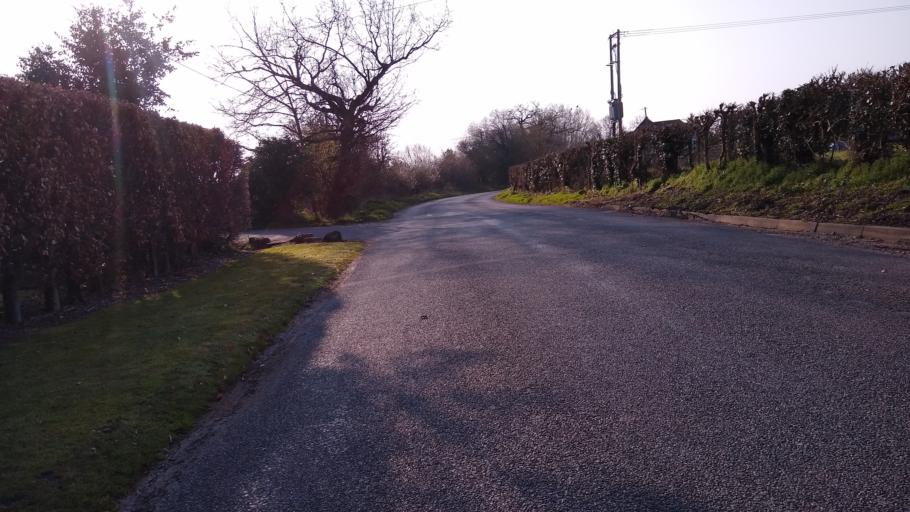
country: GB
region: England
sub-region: Wokingham
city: Winnersh
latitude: 51.4403
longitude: -0.8625
